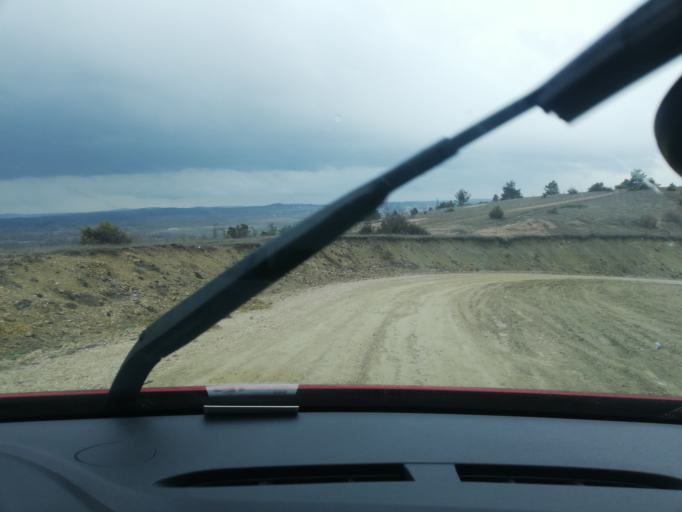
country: TR
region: Kastamonu
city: Seydiler
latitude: 41.6259
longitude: 33.7262
